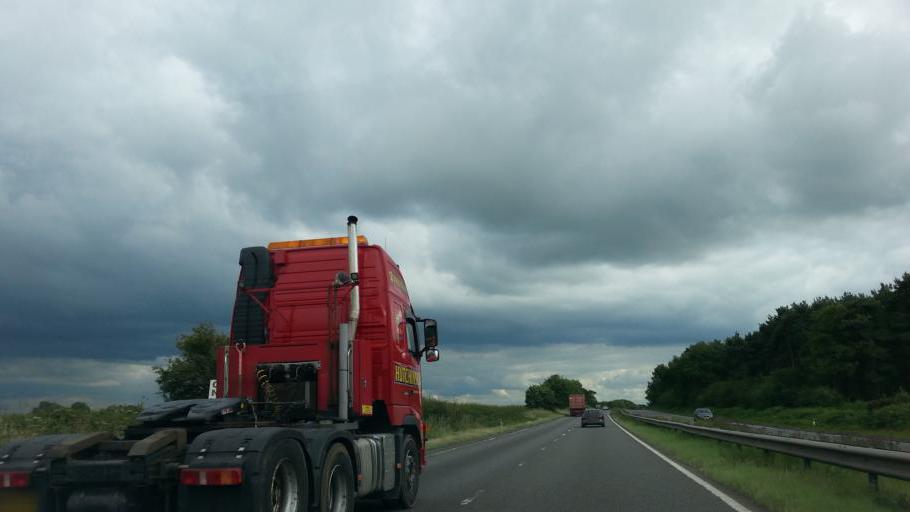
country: GB
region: England
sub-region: Nottinghamshire
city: Bircotes
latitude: 53.3595
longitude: -1.0459
